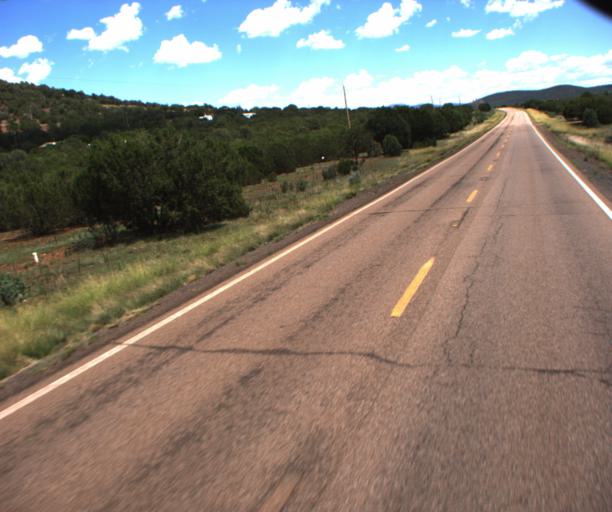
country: US
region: Arizona
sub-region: Navajo County
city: White Mountain Lake
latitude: 34.2787
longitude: -109.7987
